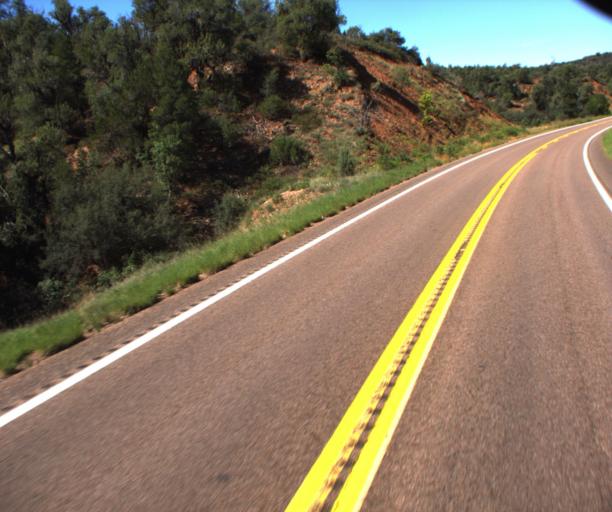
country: US
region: Arizona
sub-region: Navajo County
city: Cibecue
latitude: 34.0131
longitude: -110.2442
